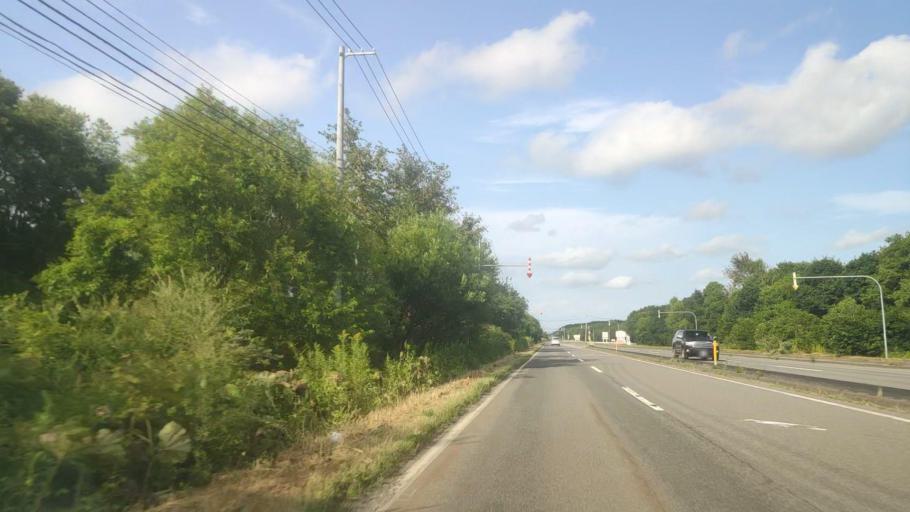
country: JP
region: Hokkaido
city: Tomakomai
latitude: 42.6834
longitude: 141.7197
